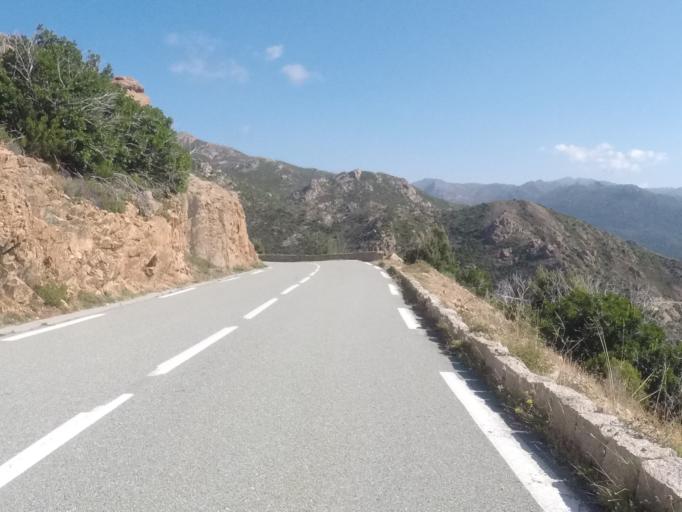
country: FR
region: Corsica
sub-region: Departement de la Corse-du-Sud
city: Olmeto
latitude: 41.7651
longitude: 9.0415
